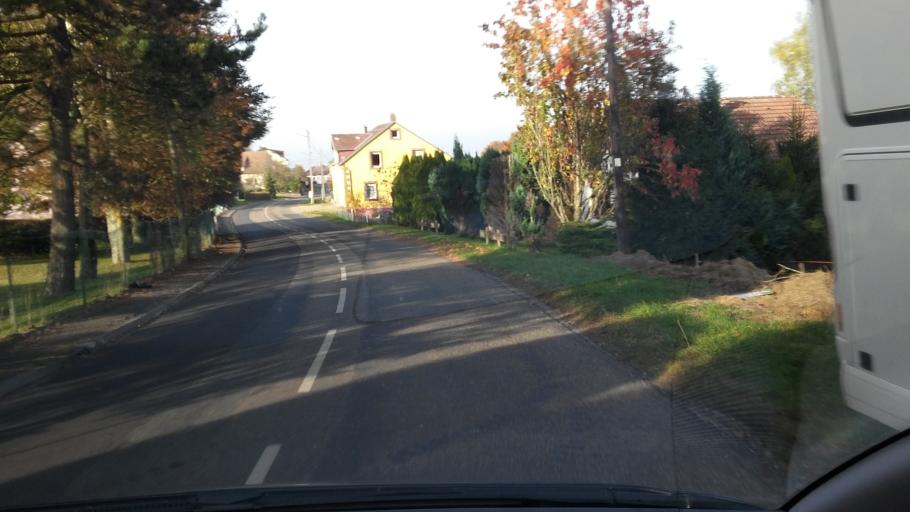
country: FR
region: Alsace
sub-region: Departement du Bas-Rhin
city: Wangenbourg-Engenthal
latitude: 48.6470
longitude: 7.2760
